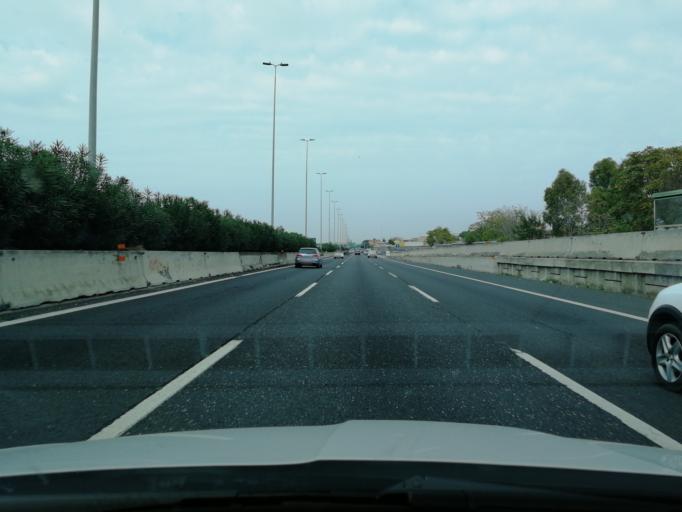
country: IT
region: Latium
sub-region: Citta metropolitana di Roma Capitale
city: Ciampino
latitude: 41.8545
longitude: 12.5979
